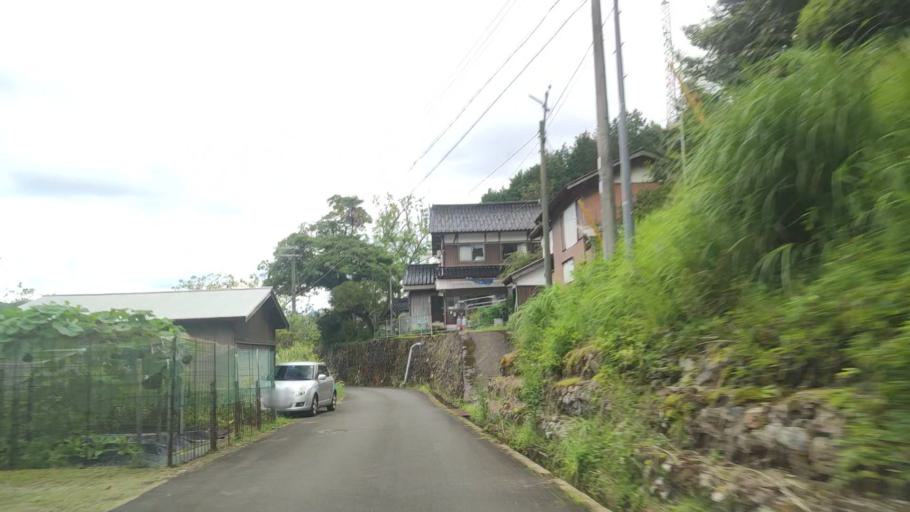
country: JP
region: Hyogo
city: Toyooka
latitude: 35.5994
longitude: 134.8810
